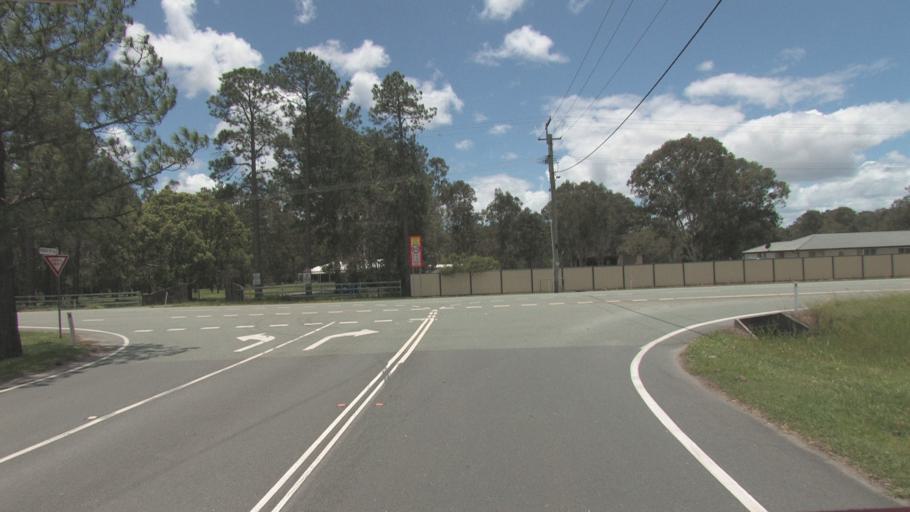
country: AU
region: Queensland
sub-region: Gold Coast
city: Yatala
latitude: -27.6778
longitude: 153.2364
